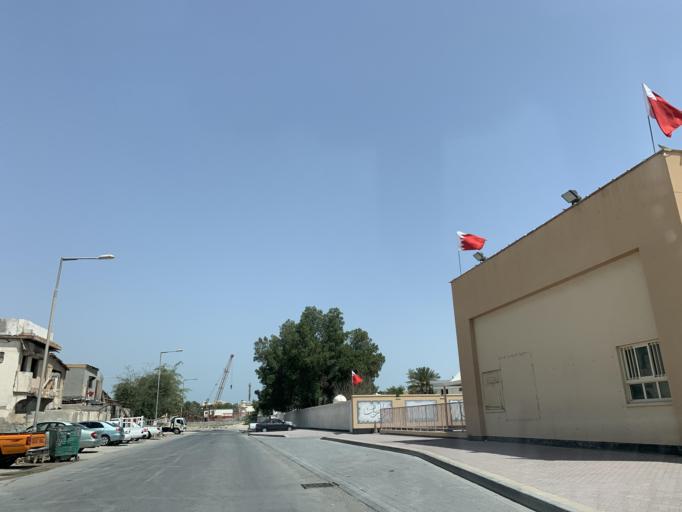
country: BH
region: Northern
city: Sitrah
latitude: 26.1390
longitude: 50.6066
